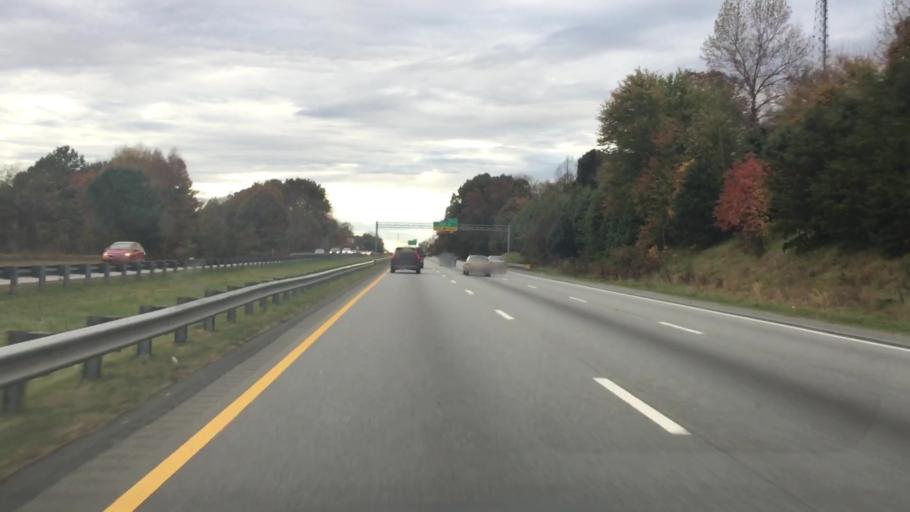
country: US
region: North Carolina
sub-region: Forsyth County
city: Winston-Salem
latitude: 36.0991
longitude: -80.2034
